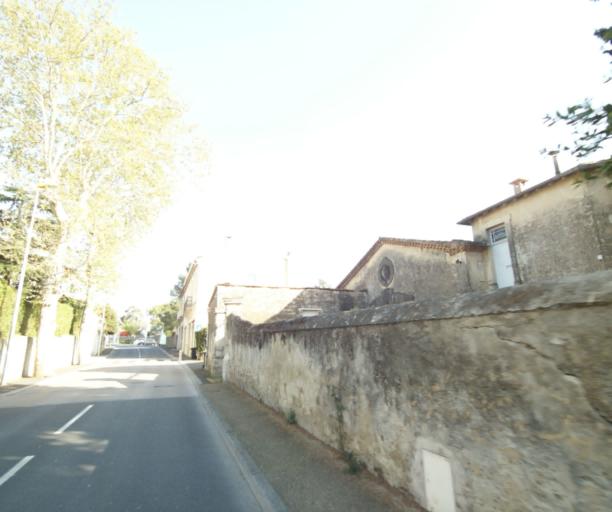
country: FR
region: Languedoc-Roussillon
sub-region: Departement de l'Herault
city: Juvignac
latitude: 43.6095
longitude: 3.7877
